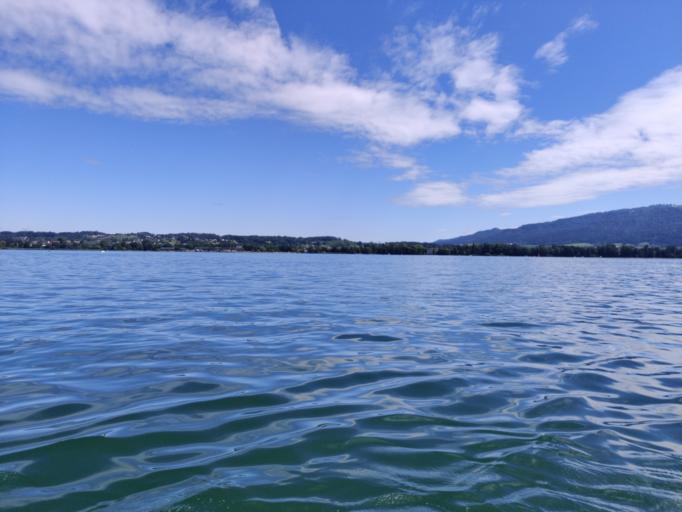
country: DE
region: Bavaria
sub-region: Swabia
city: Lindau
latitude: 47.5358
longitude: 9.7070
